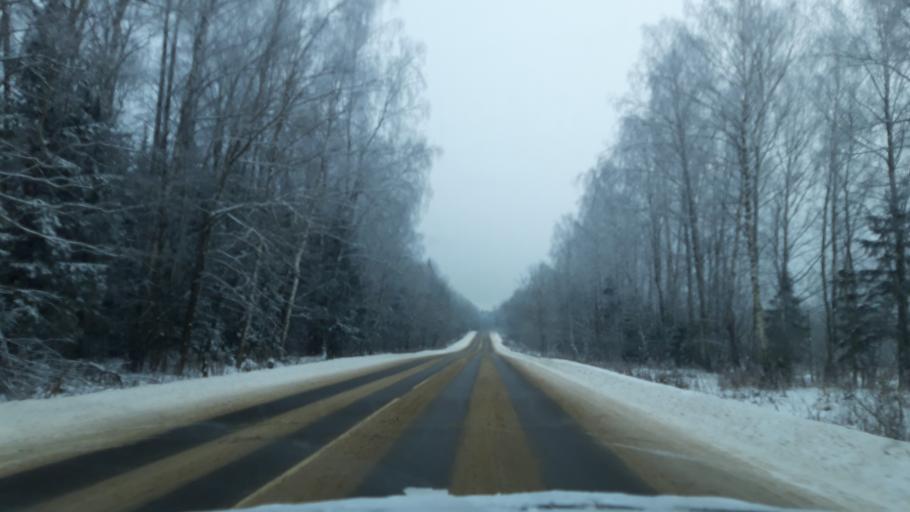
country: RU
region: Moskovskaya
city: Avtopoligon
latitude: 56.2758
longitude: 37.3680
